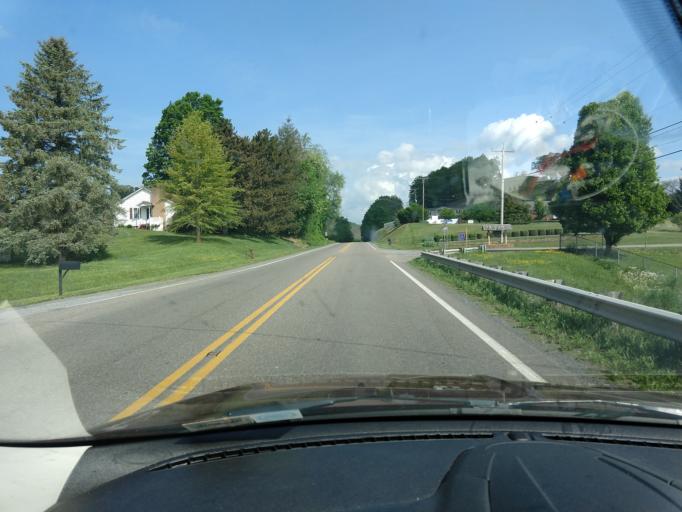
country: US
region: Virginia
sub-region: Russell County
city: Honaker
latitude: 36.9664
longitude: -81.9379
